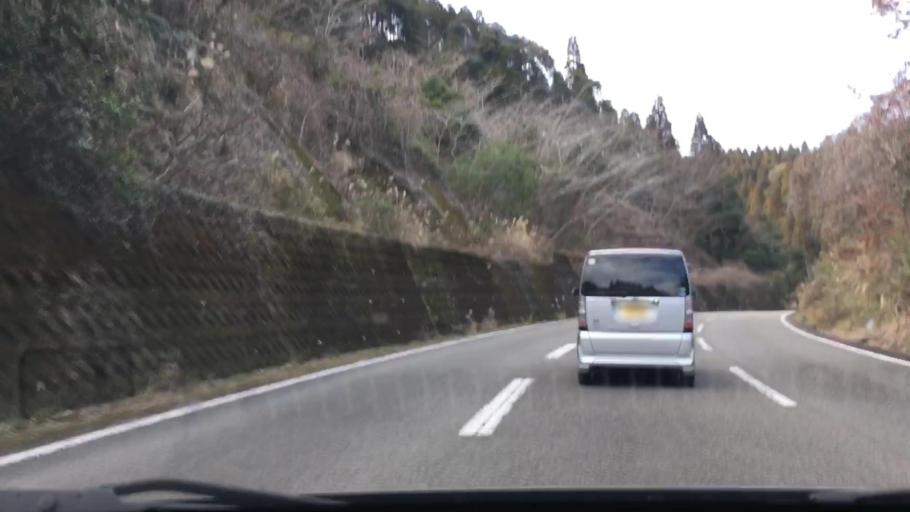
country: JP
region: Miyazaki
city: Nichinan
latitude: 31.6304
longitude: 131.3393
